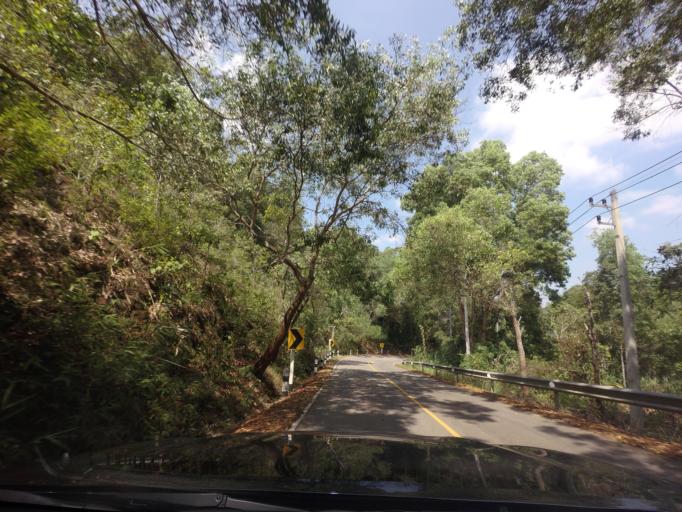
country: TH
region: Loei
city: Na Haeo
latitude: 17.4918
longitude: 100.9012
